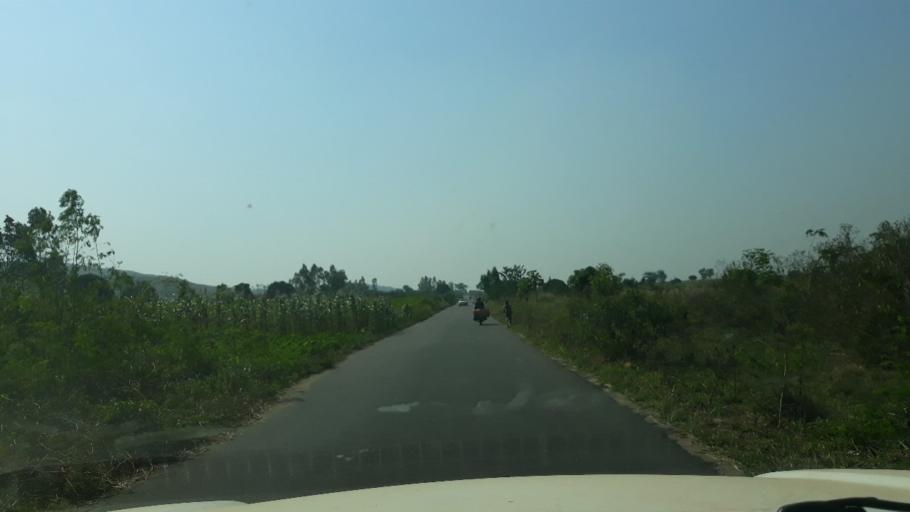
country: CD
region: South Kivu
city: Uvira
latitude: -3.2148
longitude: 29.1647
